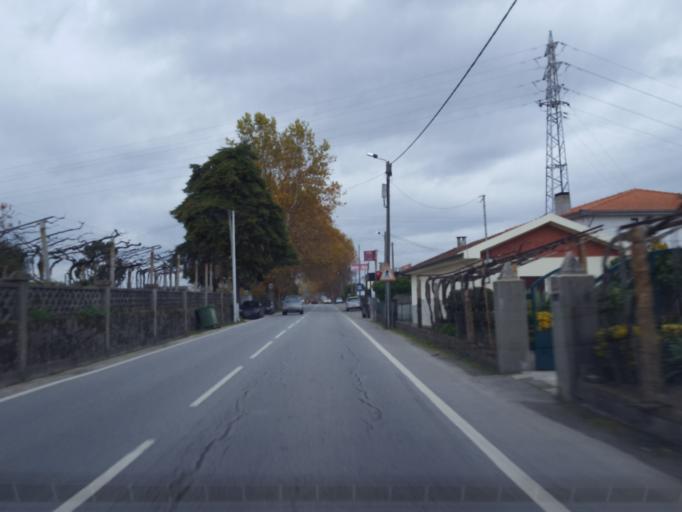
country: PT
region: Porto
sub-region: Marco de Canaveses
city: Marco de Canavezes
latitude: 41.1713
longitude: -8.1512
